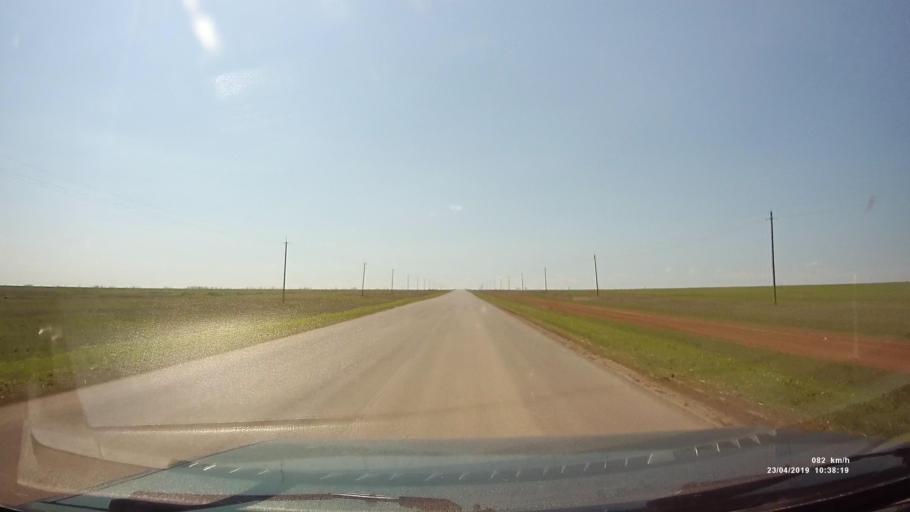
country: RU
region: Kalmykiya
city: Yashalta
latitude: 46.5344
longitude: 42.6388
